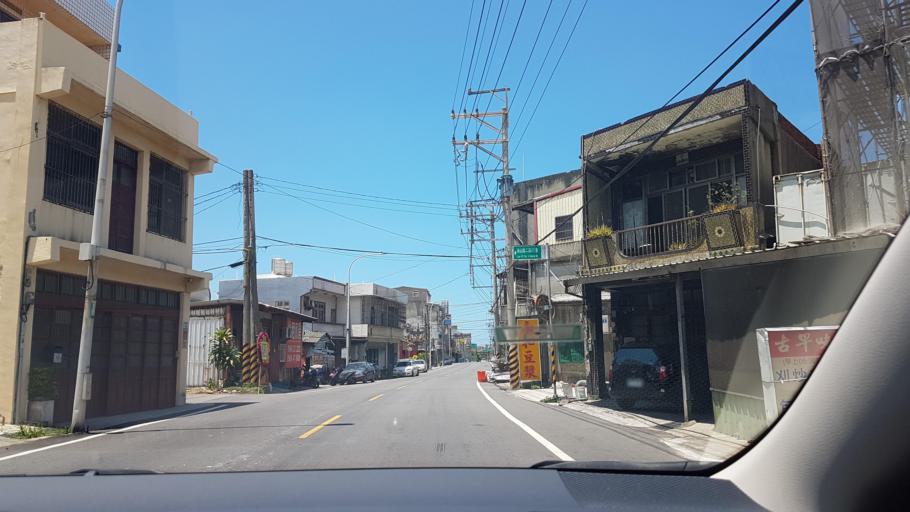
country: TW
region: Taiwan
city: Taoyuan City
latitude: 25.1094
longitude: 121.2554
